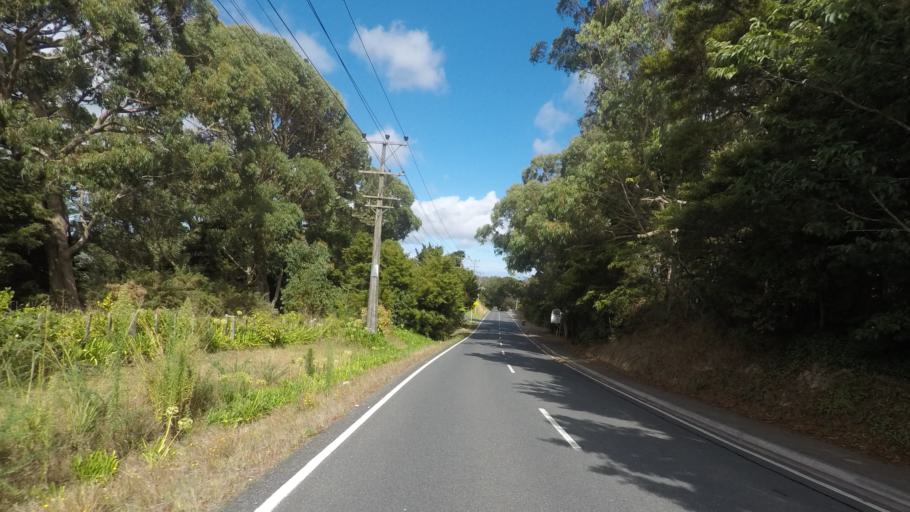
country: NZ
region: Auckland
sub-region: Auckland
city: Muriwai Beach
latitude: -36.7692
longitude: 174.5525
